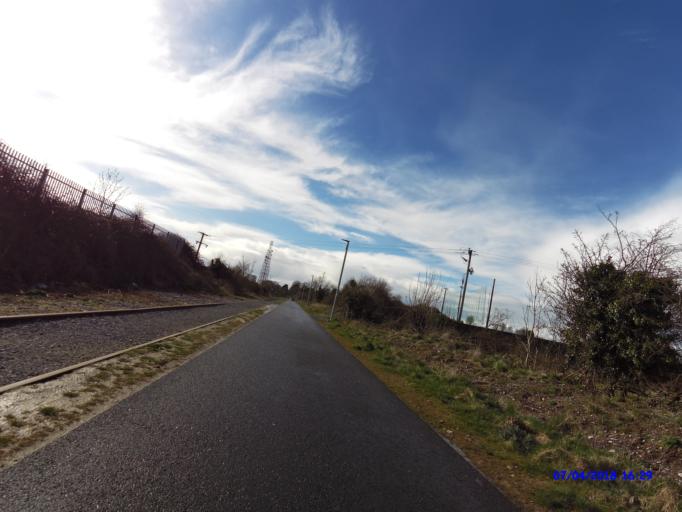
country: IE
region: Leinster
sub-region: An Iarmhi
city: Athlone
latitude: 53.4269
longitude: -7.9249
